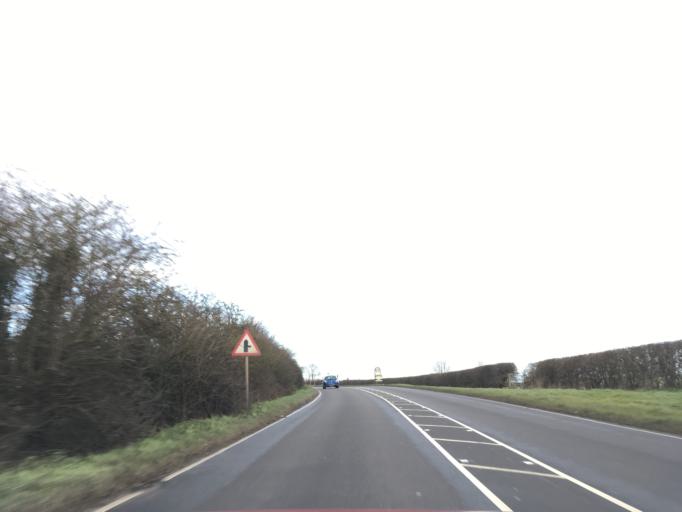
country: GB
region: England
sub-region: Nottinghamshire
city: Ruddington
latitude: 52.8716
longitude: -1.1309
